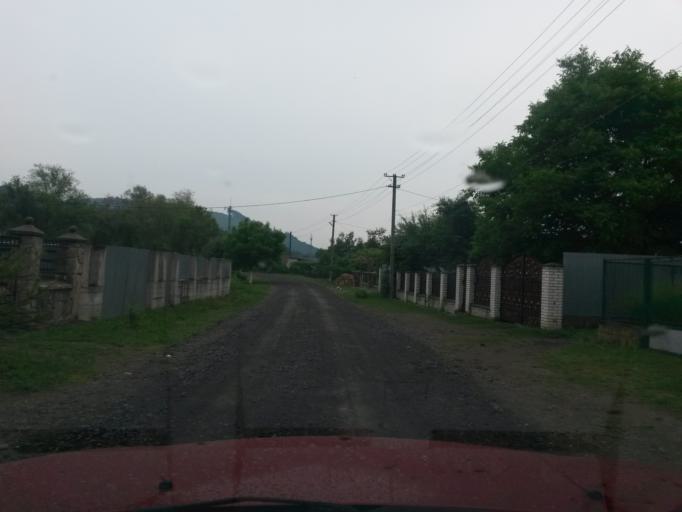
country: UA
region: Zakarpattia
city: Velykyi Bereznyi
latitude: 48.9041
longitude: 22.4650
